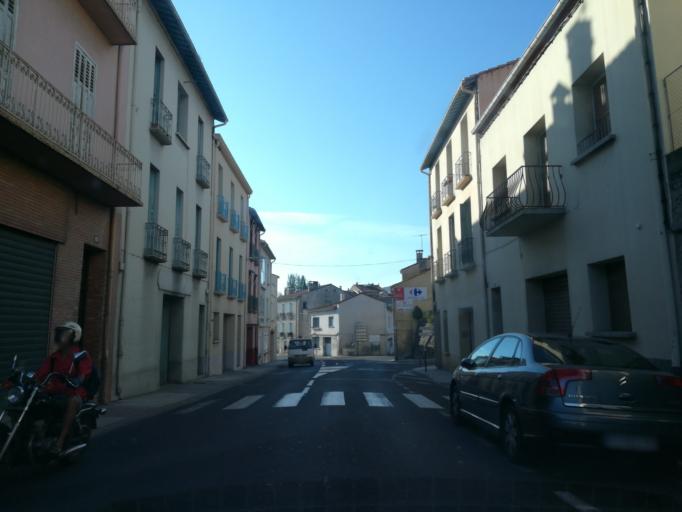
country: FR
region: Languedoc-Roussillon
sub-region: Departement des Pyrenees-Orientales
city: Ceret
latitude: 42.4899
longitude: 2.7457
